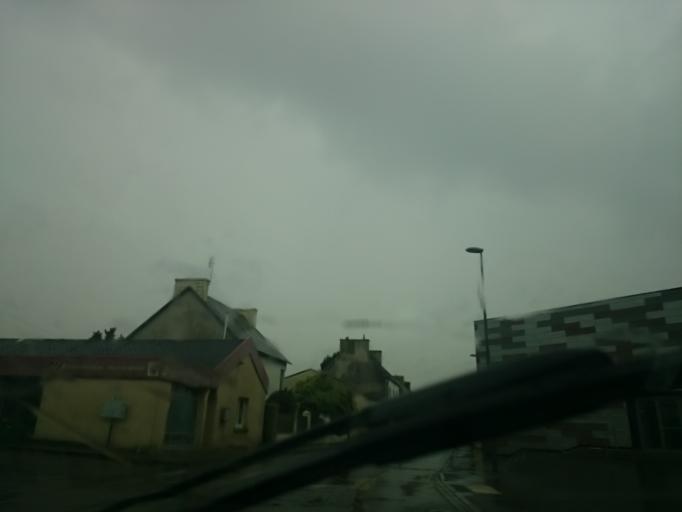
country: FR
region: Brittany
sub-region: Departement du Finistere
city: Plouvien
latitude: 48.5310
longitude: -4.4496
